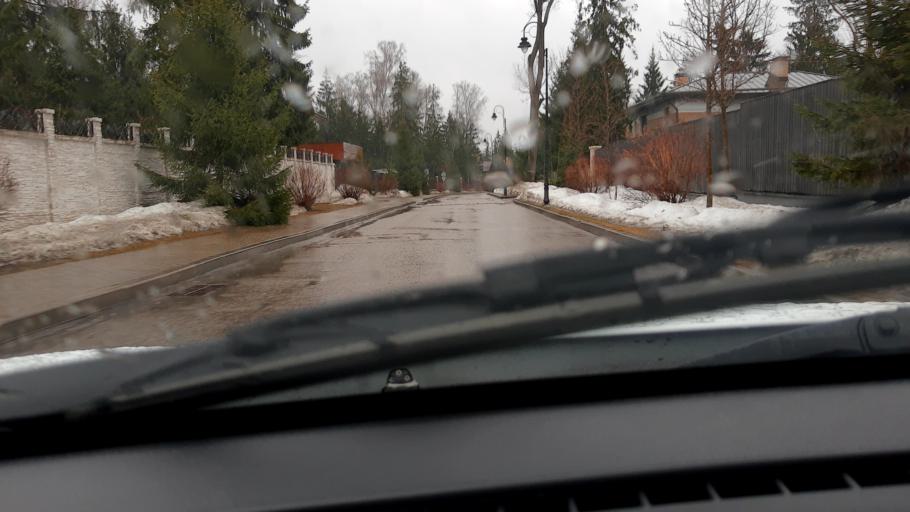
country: RU
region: Moskovskaya
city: Moskovskiy
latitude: 55.5806
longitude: 37.3959
